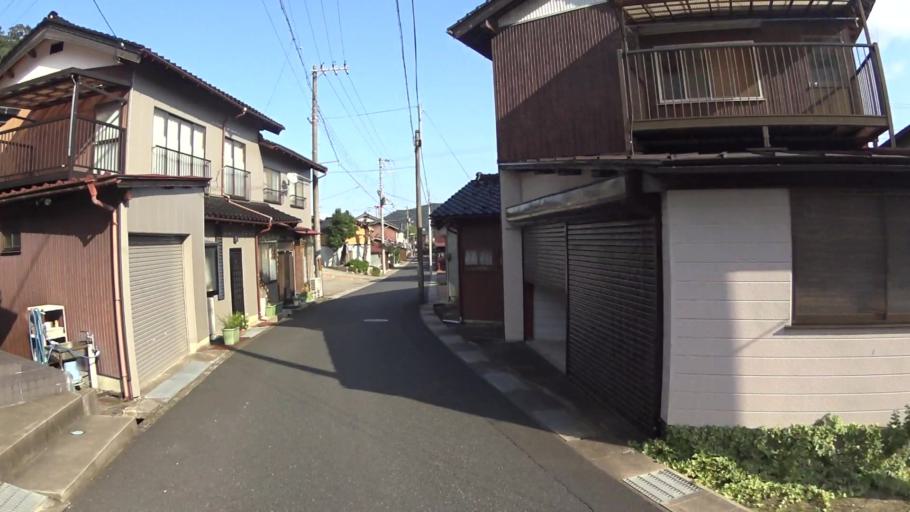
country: JP
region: Kyoto
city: Miyazu
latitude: 35.5638
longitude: 135.1457
